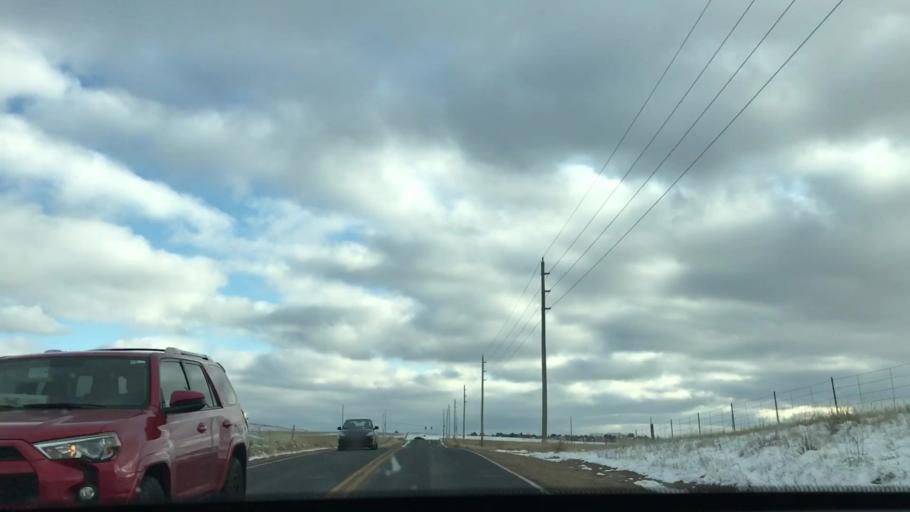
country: US
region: Colorado
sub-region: Boulder County
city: Lafayette
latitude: 39.9612
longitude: -105.0720
